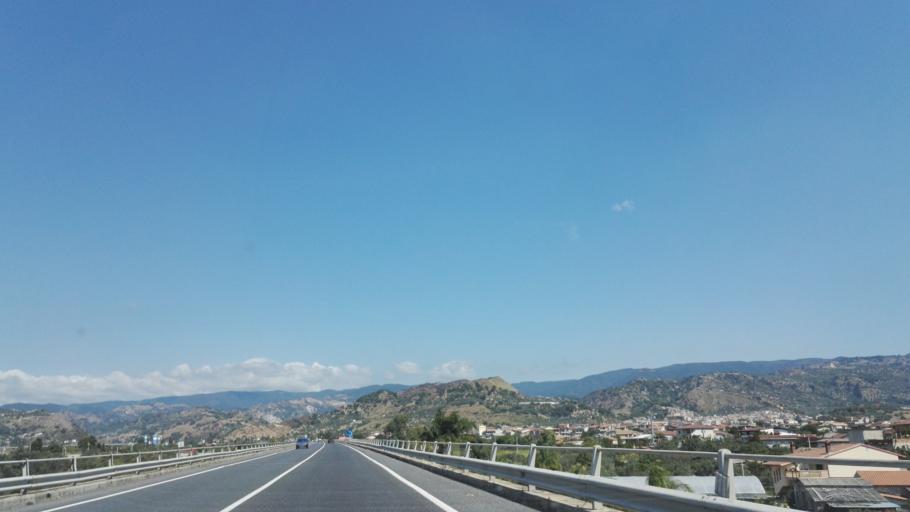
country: IT
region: Calabria
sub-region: Provincia di Reggio Calabria
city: Gioiosa Ionica
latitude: 38.3149
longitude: 16.3018
